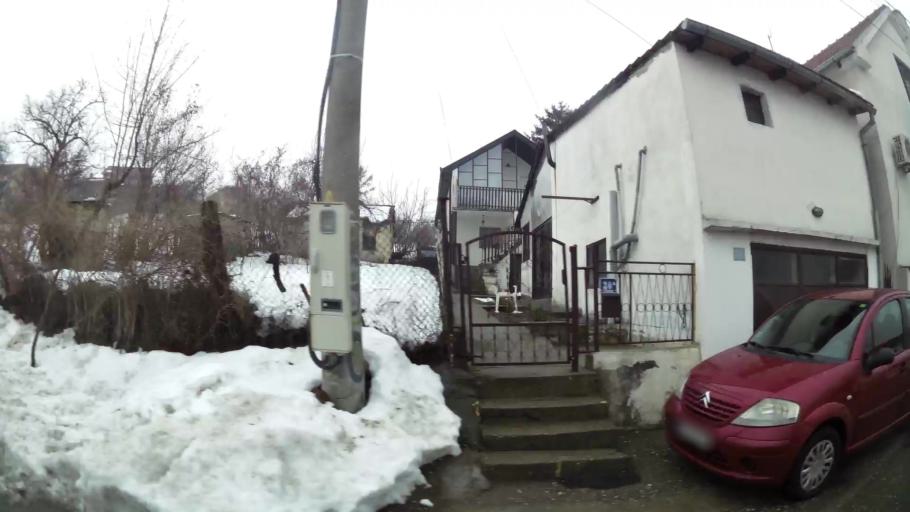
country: RS
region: Central Serbia
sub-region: Belgrade
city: Zvezdara
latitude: 44.7579
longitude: 20.5204
